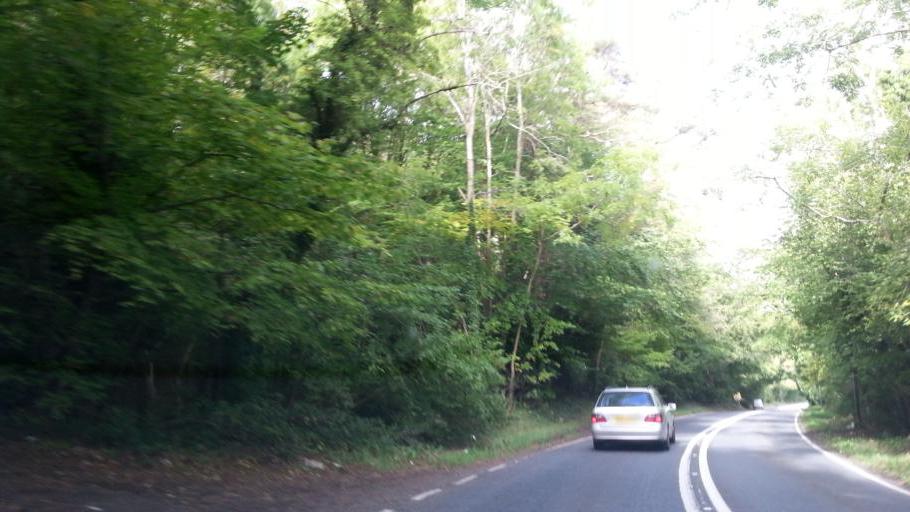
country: GB
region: England
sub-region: Gloucestershire
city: Painswick
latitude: 51.8004
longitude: -2.1923
